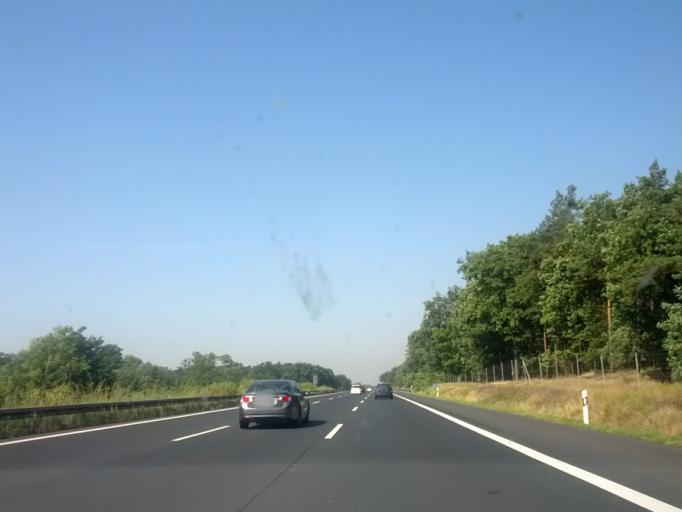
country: DE
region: Brandenburg
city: Rangsdorf
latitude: 52.3068
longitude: 13.3902
